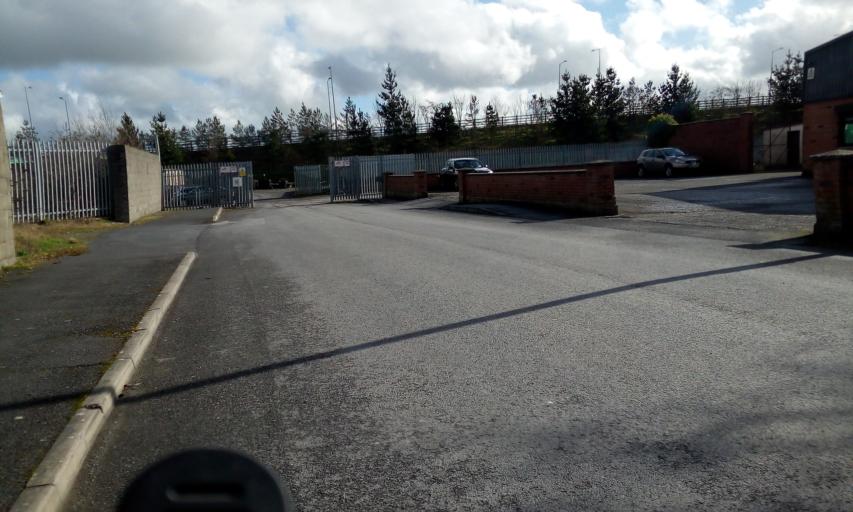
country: IE
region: Leinster
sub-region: Kilkenny
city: Kilkenny
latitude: 52.6559
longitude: -7.2272
